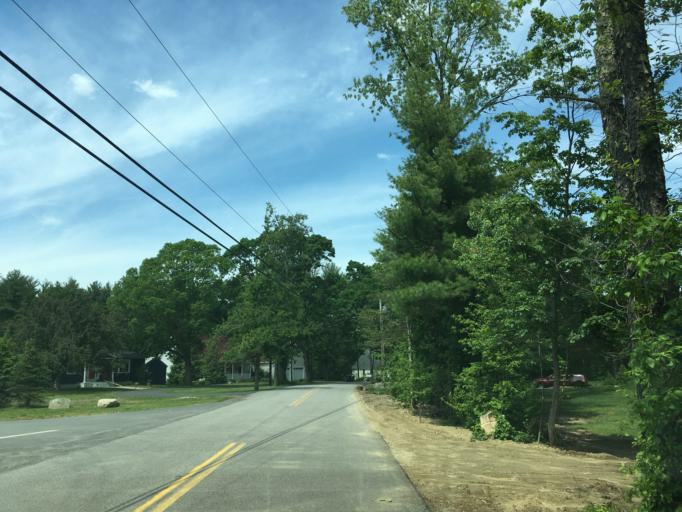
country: US
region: New Hampshire
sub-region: Rockingham County
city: Stratham Station
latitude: 43.0334
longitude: -70.8712
